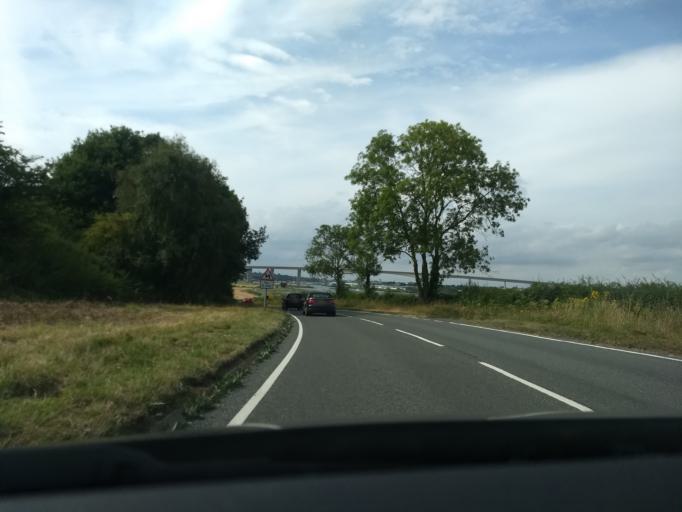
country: GB
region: England
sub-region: Suffolk
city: Ipswich
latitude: 52.0163
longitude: 1.1679
